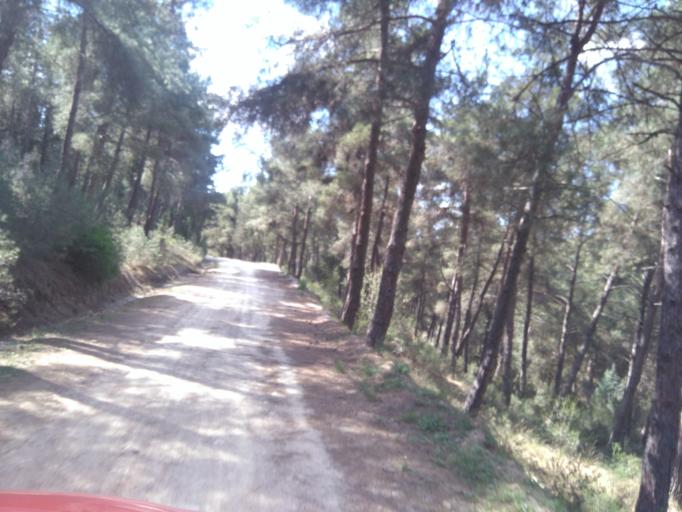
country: GR
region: Central Macedonia
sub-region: Nomos Thessalonikis
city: Pefka
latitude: 40.6478
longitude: 22.9802
